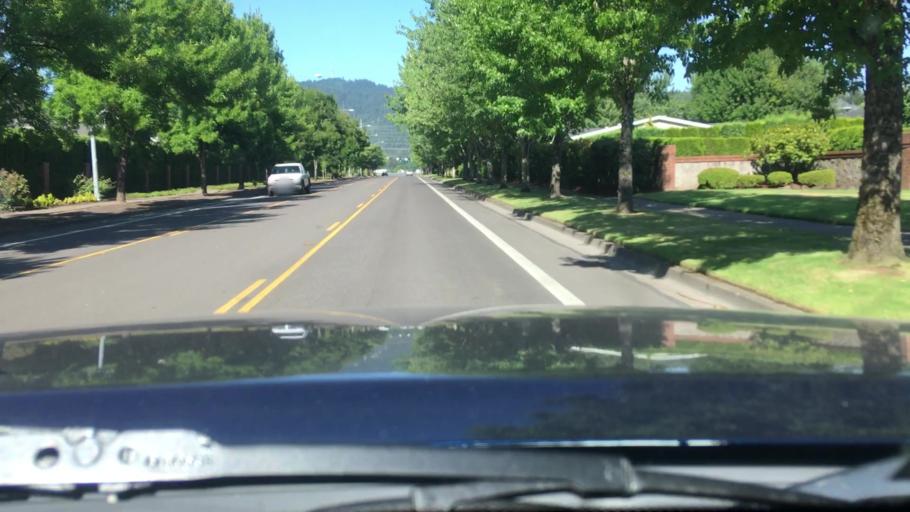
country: US
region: Oregon
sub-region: Lane County
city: Coburg
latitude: 44.0933
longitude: -123.0557
